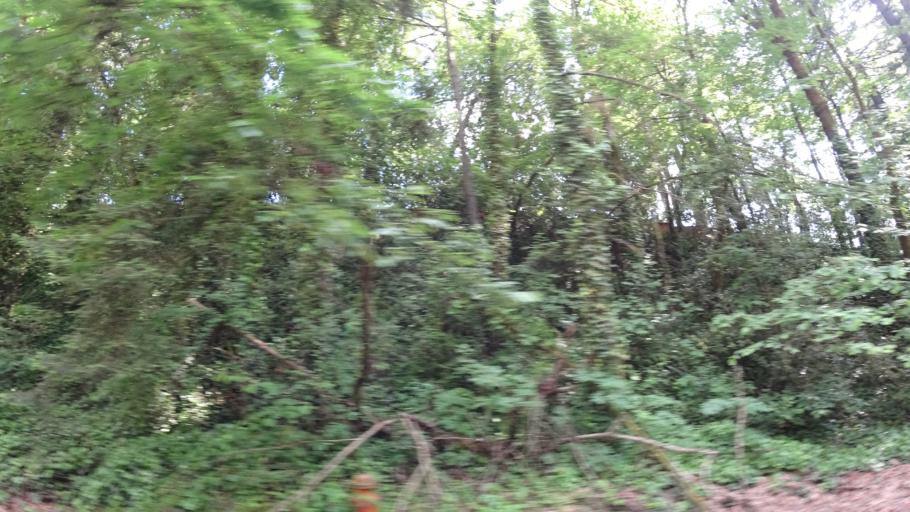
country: US
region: Oregon
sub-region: Washington County
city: Garden Home-Whitford
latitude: 45.4675
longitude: -122.7268
